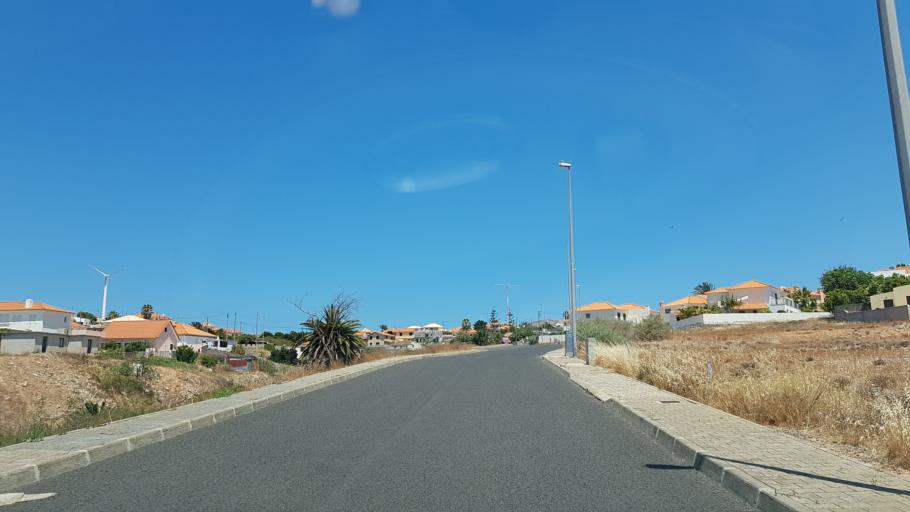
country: PT
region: Madeira
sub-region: Porto Santo
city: Vila de Porto Santo
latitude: 33.0558
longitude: -16.3547
